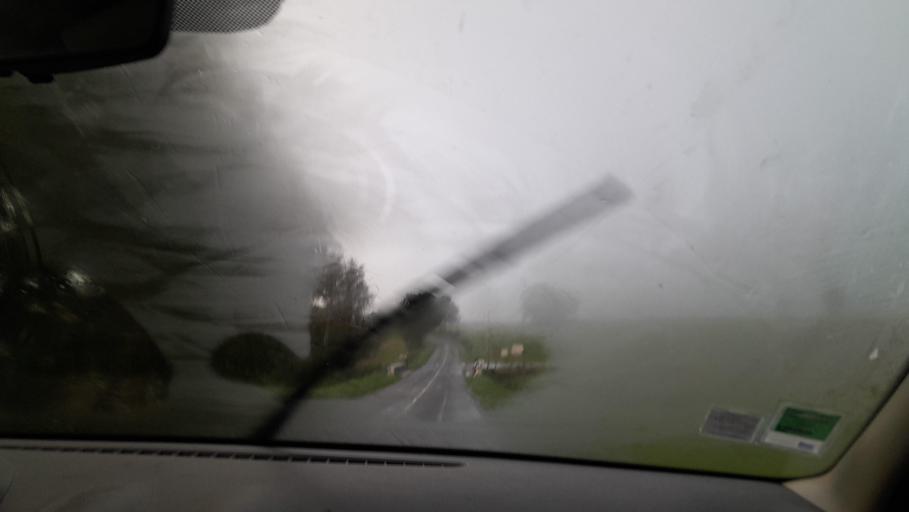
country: FR
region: Pays de la Loire
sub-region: Departement de la Mayenne
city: Ballots
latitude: 47.8645
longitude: -1.0489
